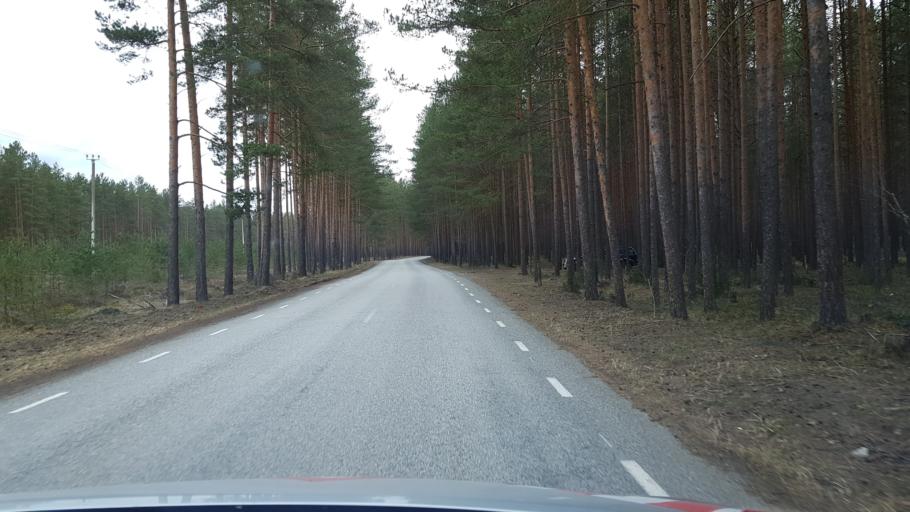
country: EE
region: Ida-Virumaa
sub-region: Narva-Joesuu linn
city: Narva-Joesuu
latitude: 59.4240
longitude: 28.1171
